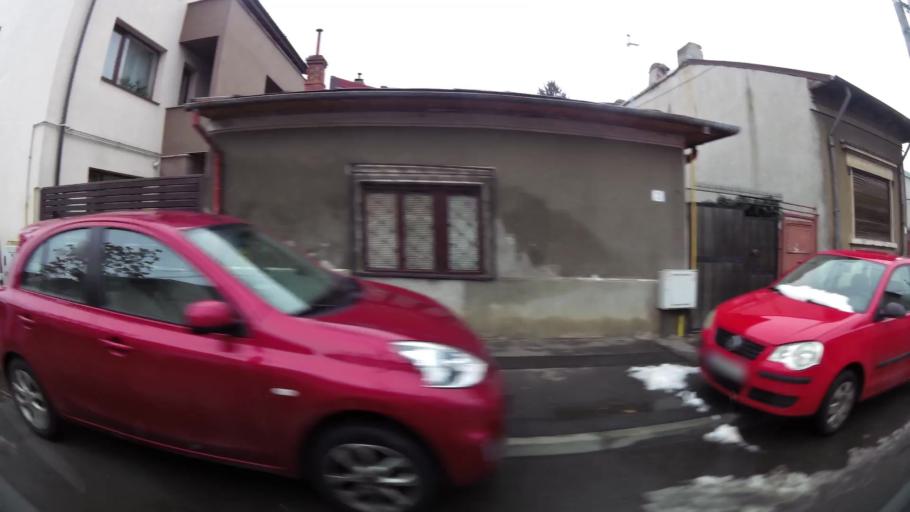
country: RO
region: Bucuresti
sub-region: Municipiul Bucuresti
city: Bucuresti
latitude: 44.4537
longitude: 26.0700
